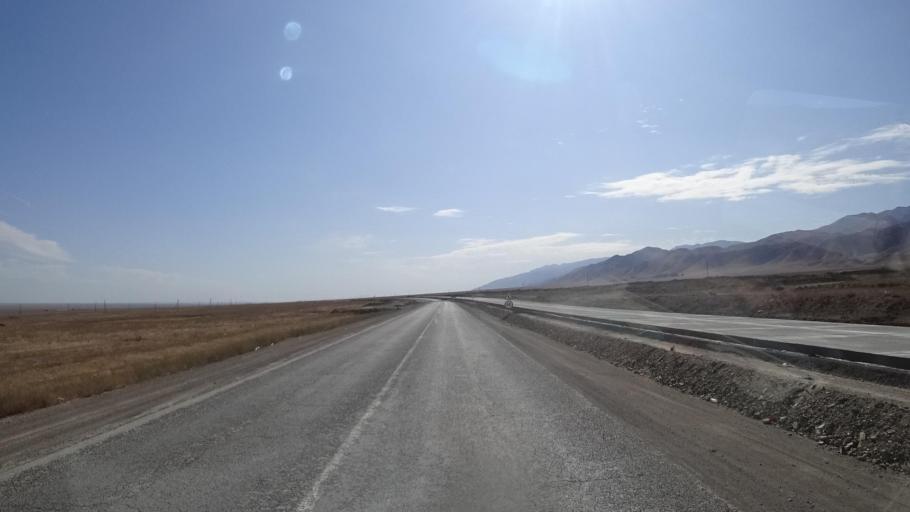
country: KG
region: Chuy
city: Ivanovka
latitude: 43.3882
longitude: 75.1481
